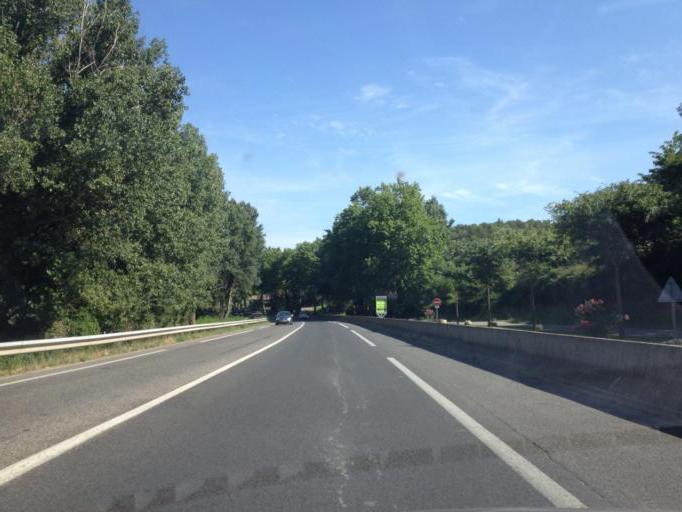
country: FR
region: Provence-Alpes-Cote d'Azur
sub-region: Departement du Vaucluse
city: Mornas
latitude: 44.2082
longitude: 4.7276
